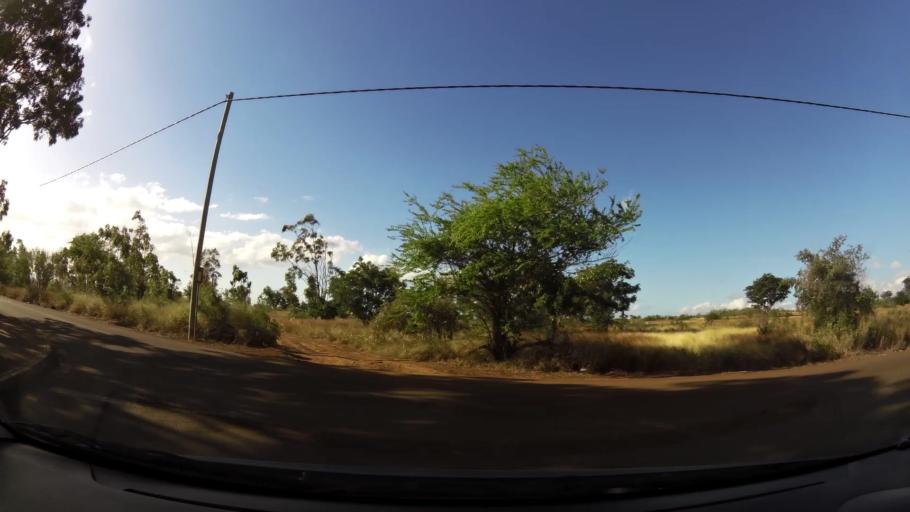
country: MU
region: Black River
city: Gros Cailloux
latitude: -20.1931
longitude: 57.4130
